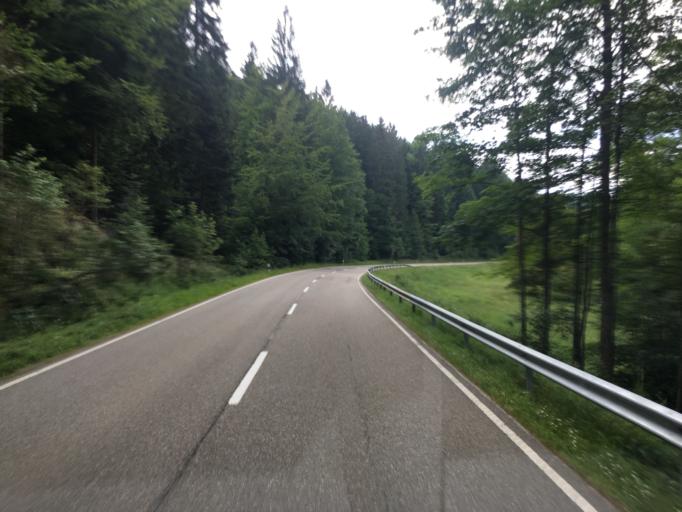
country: DE
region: Baden-Wuerttemberg
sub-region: Karlsruhe Region
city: Buhlertal
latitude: 48.6798
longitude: 8.2336
